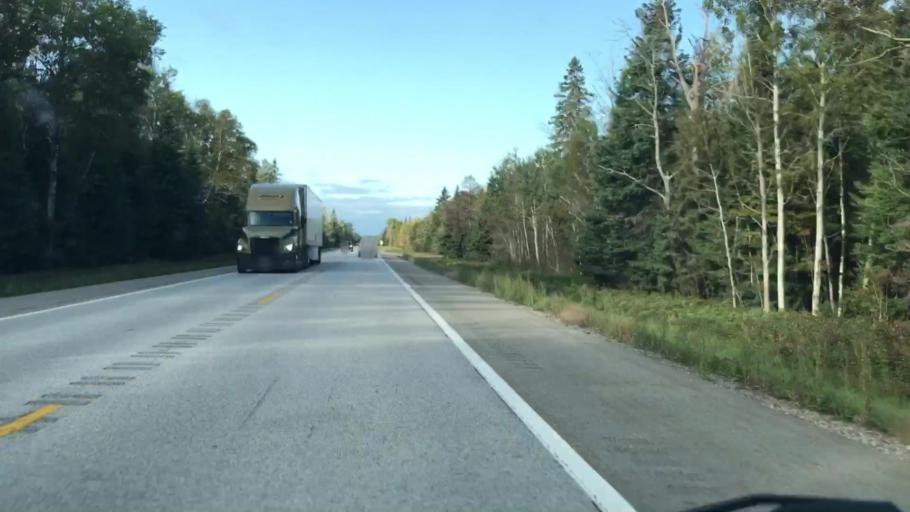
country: US
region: Michigan
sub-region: Luce County
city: Newberry
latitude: 46.3285
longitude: -85.1586
